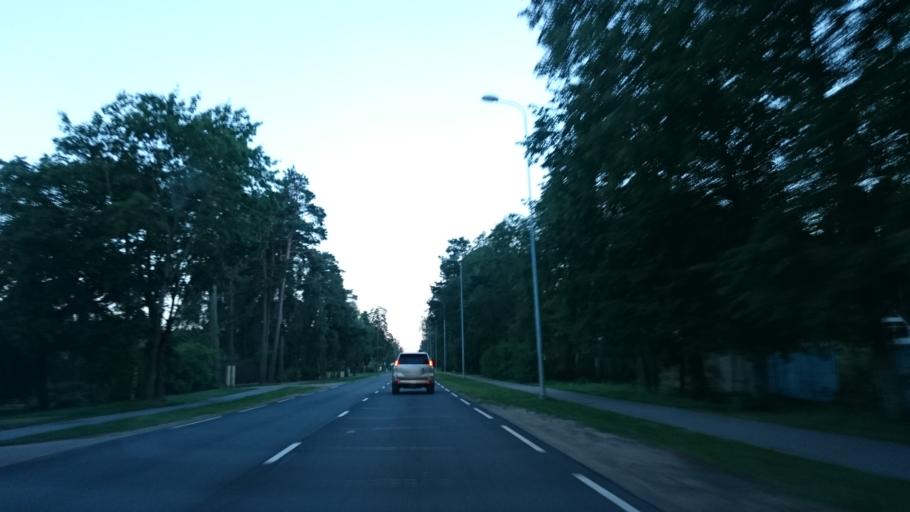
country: LV
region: Saulkrastu
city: Saulkrasti
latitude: 57.2462
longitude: 24.4048
